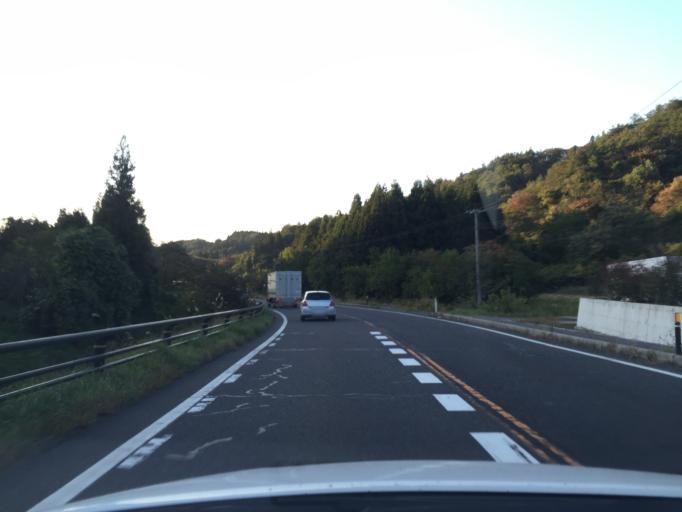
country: JP
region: Fukushima
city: Sukagawa
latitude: 37.2990
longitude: 140.5150
